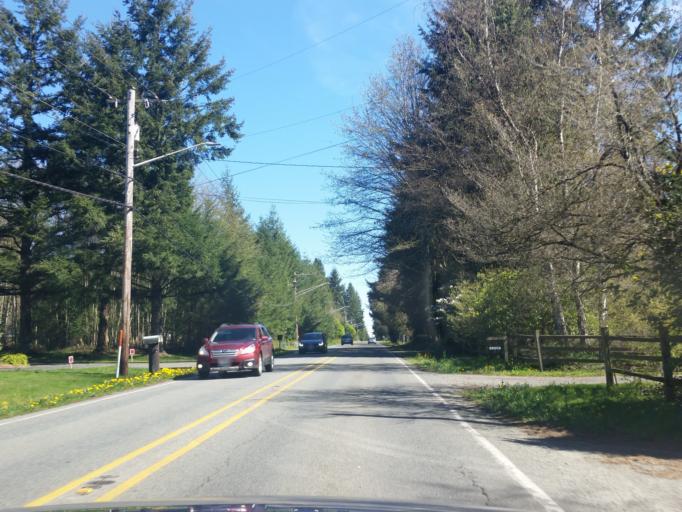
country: US
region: Washington
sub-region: Snohomish County
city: Clearview
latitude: 47.8341
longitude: -122.1472
